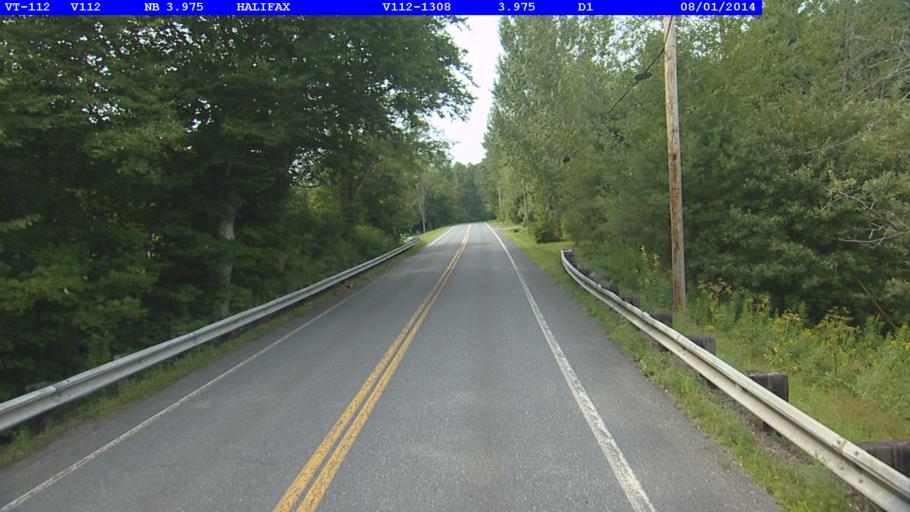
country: US
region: Massachusetts
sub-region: Franklin County
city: Colrain
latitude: 42.7618
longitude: -72.7811
